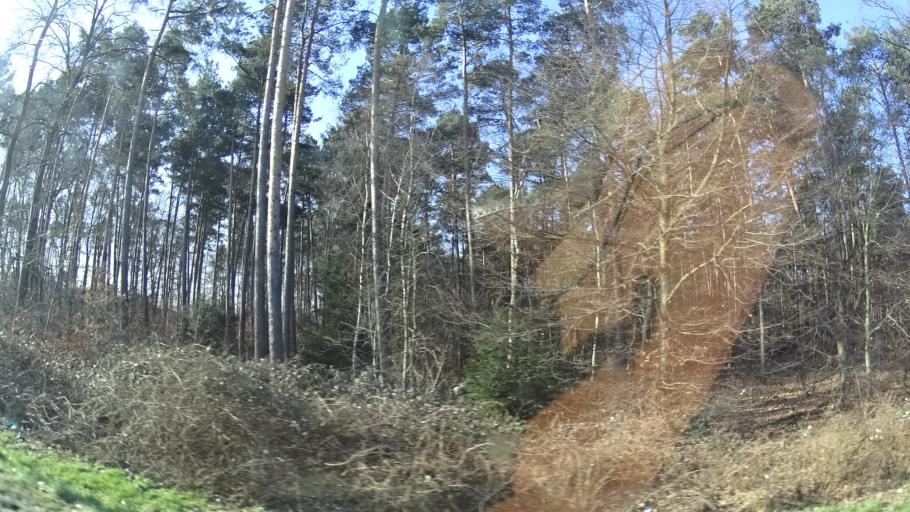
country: DE
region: Rheinland-Pfalz
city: Steinwenden
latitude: 49.4352
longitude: 7.5206
